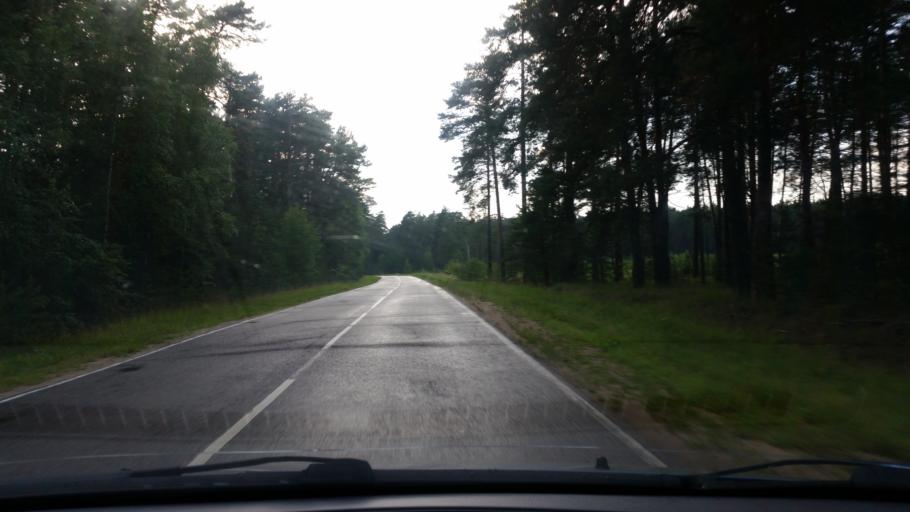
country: RU
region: Moskovskaya
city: Stupino
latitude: 54.8552
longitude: 37.8655
